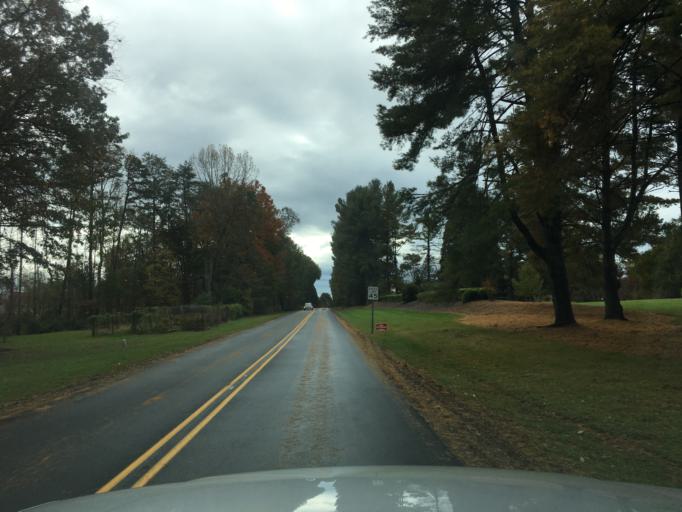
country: US
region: North Carolina
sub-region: Catawba County
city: Maiden
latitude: 35.6199
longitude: -81.2265
